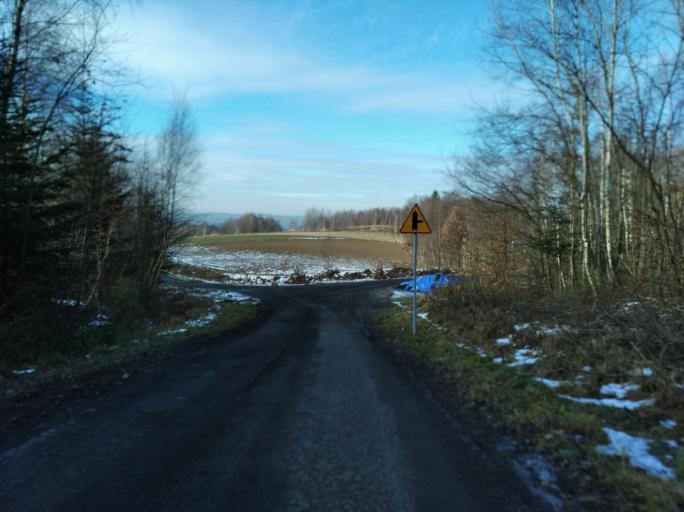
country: PL
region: Subcarpathian Voivodeship
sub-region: Powiat strzyzowski
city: Gwoznica Gorna
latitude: 49.8231
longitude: 21.9863
